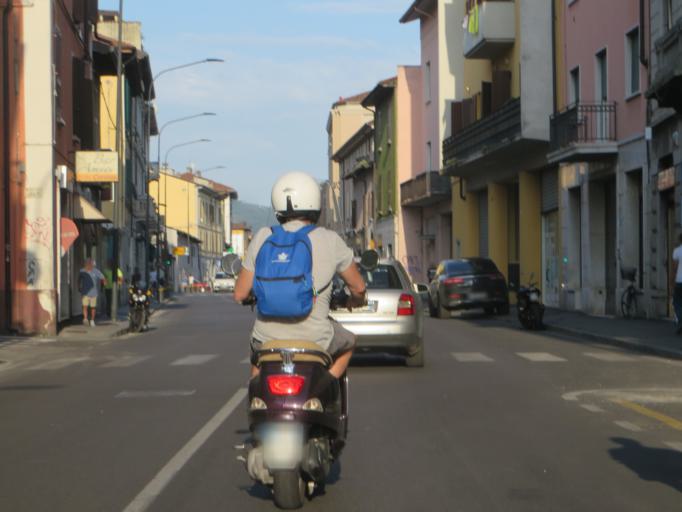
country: IT
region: Lombardy
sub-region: Provincia di Brescia
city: Brescia
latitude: 45.5459
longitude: 10.1918
